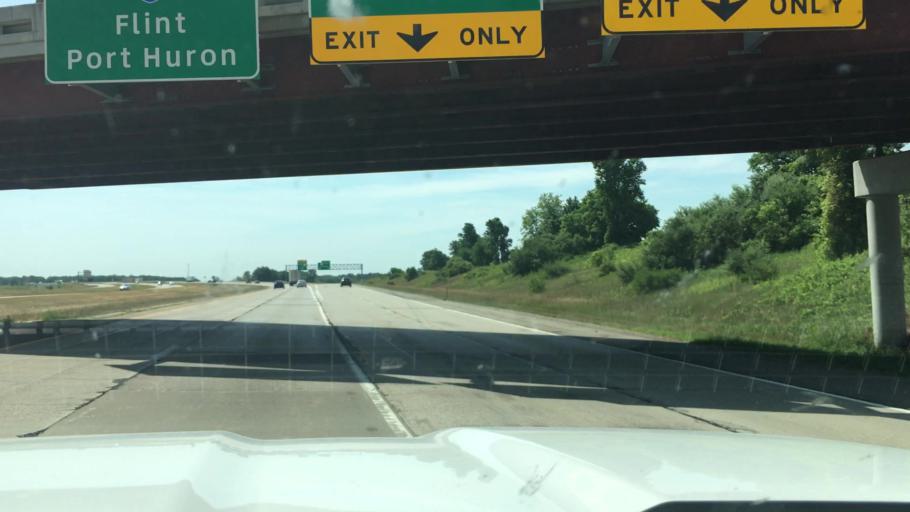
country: US
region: Michigan
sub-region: Clinton County
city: DeWitt
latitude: 42.8132
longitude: -84.5186
